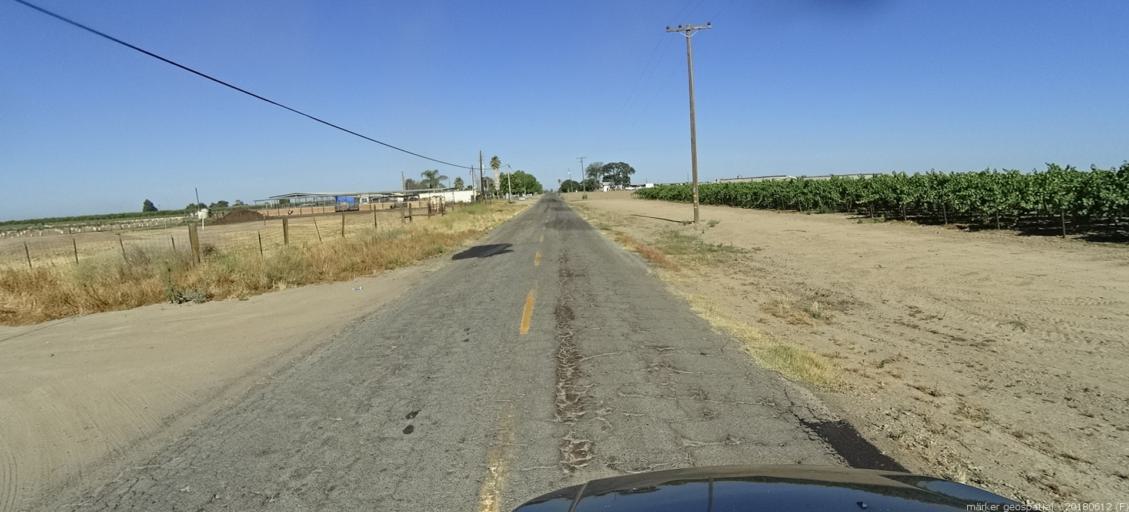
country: US
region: California
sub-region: Madera County
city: Fairmead
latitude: 37.0110
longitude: -120.1737
